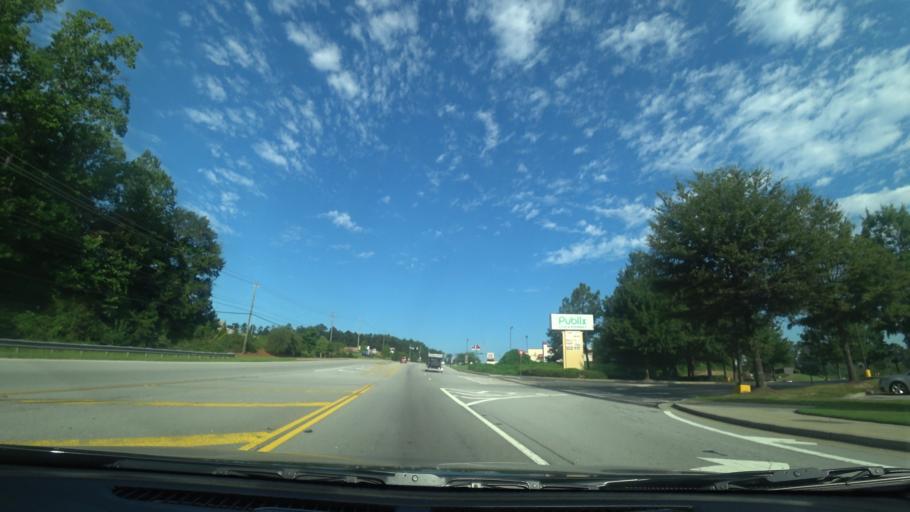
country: US
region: Georgia
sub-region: Rockdale County
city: Conyers
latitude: 33.6825
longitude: -83.9984
